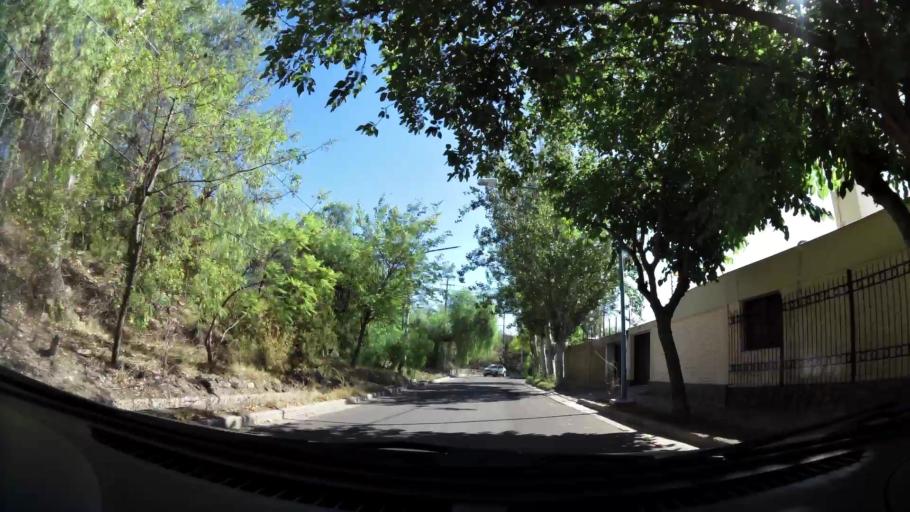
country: AR
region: Mendoza
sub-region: Departamento de Godoy Cruz
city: Godoy Cruz
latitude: -32.9021
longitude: -68.8926
